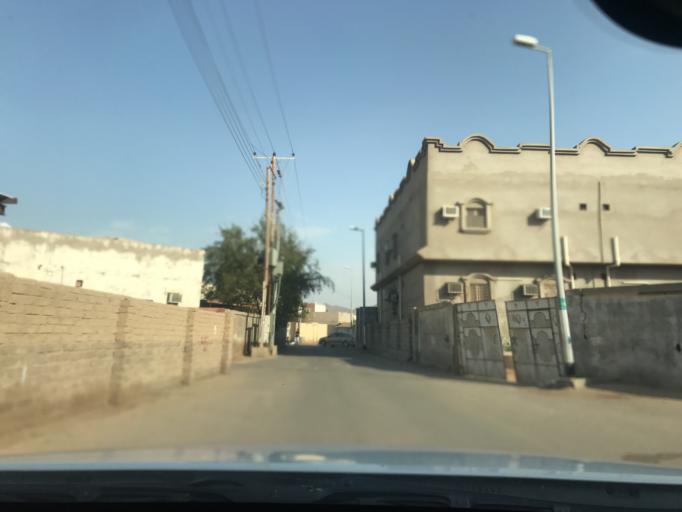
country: SA
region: Makkah
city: Al Jumum
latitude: 21.4439
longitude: 39.5345
